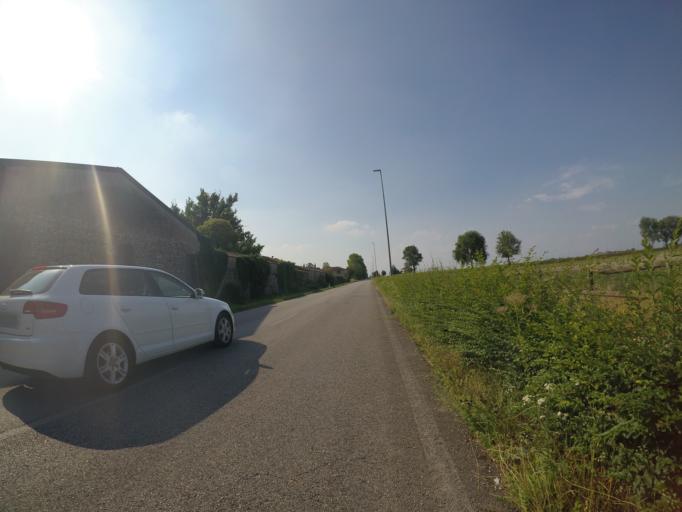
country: IT
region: Friuli Venezia Giulia
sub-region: Provincia di Udine
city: Camino al Tagliamento
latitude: 45.9297
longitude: 12.9598
